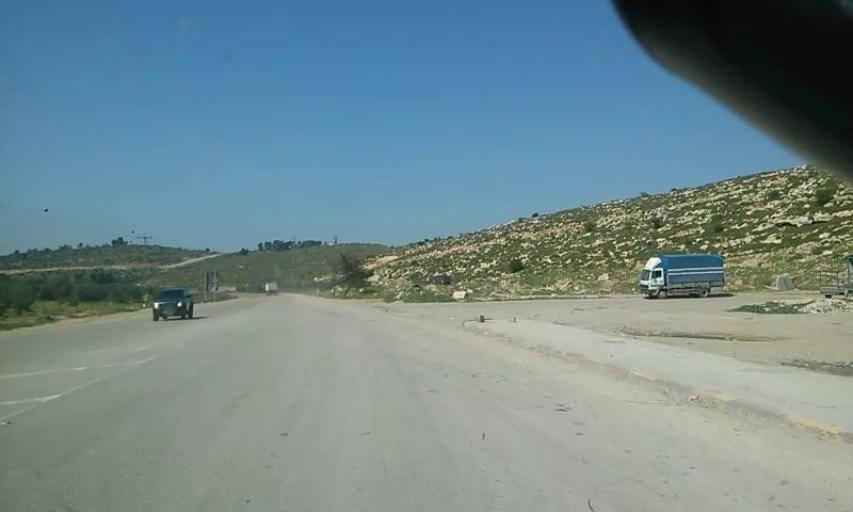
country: PS
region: West Bank
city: Idhna
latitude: 31.5850
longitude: 34.9733
